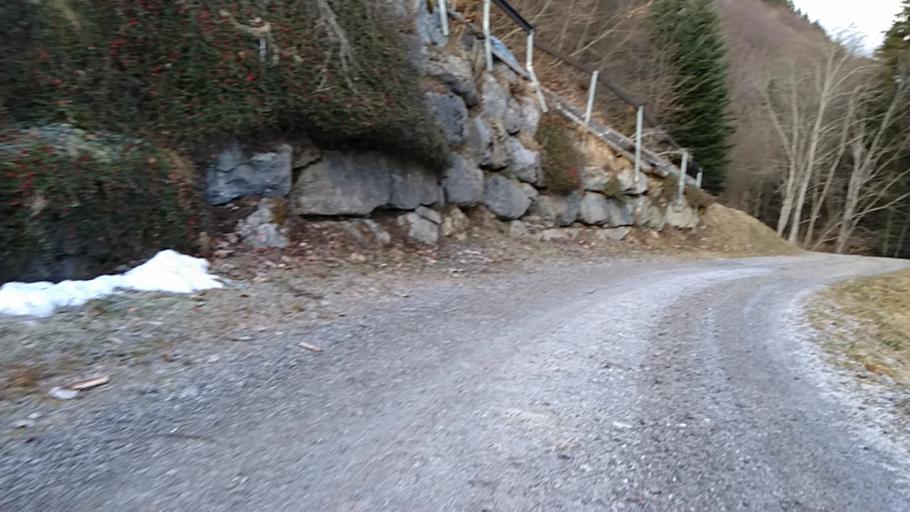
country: CH
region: Valais
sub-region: Monthey District
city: Vouvry
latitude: 46.3219
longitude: 6.8754
